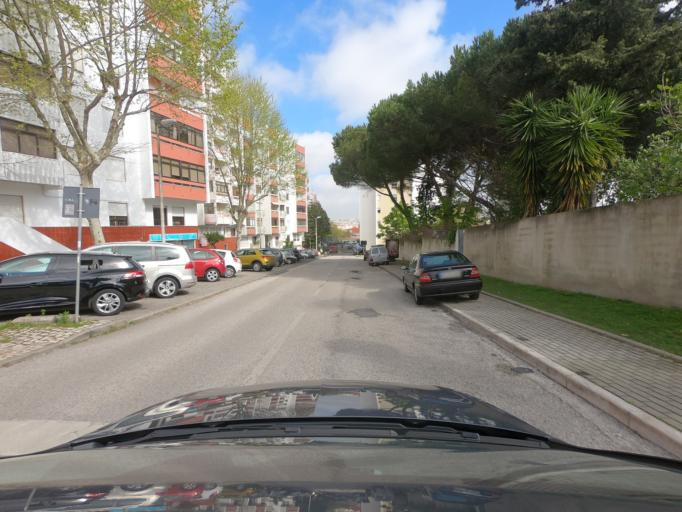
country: PT
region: Lisbon
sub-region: Amadora
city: Amadora
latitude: 38.7376
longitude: -9.2208
